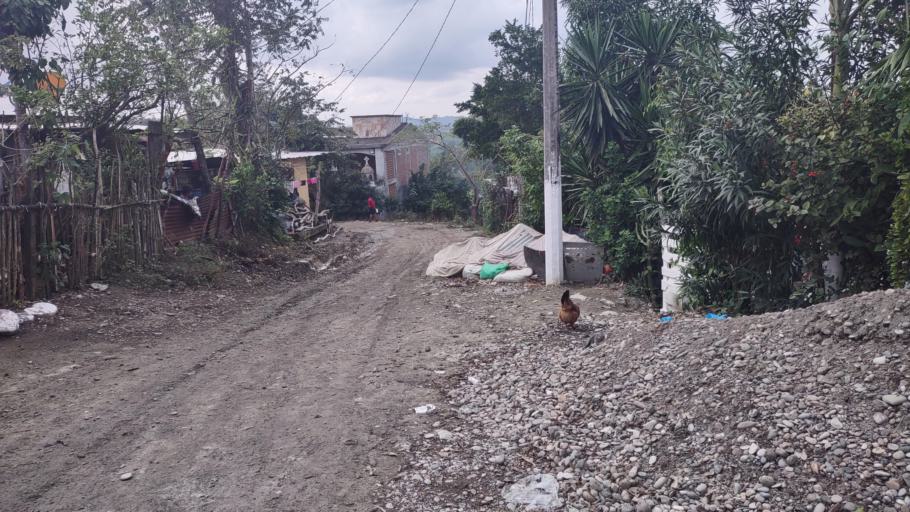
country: MX
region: Veracruz
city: Coatzintla
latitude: 20.4598
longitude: -97.4195
